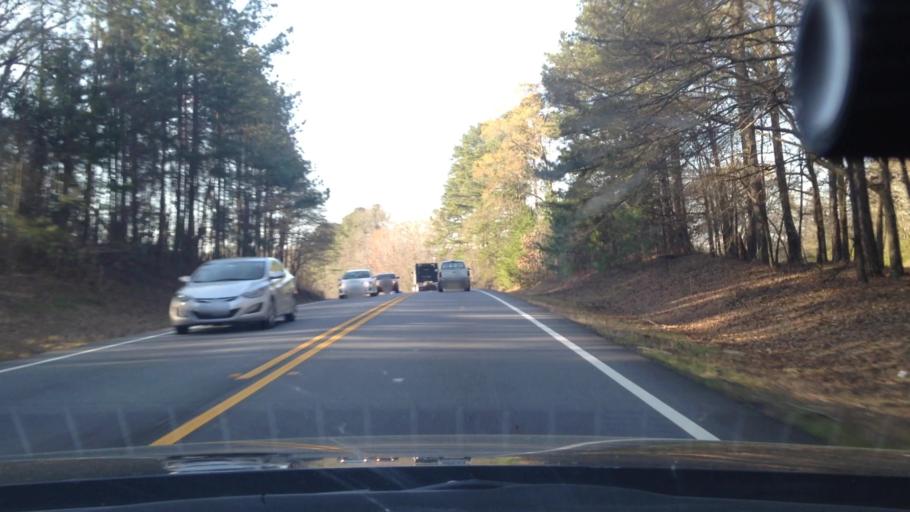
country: US
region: Georgia
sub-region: Fayette County
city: Peachtree City
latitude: 33.3355
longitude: -84.6496
